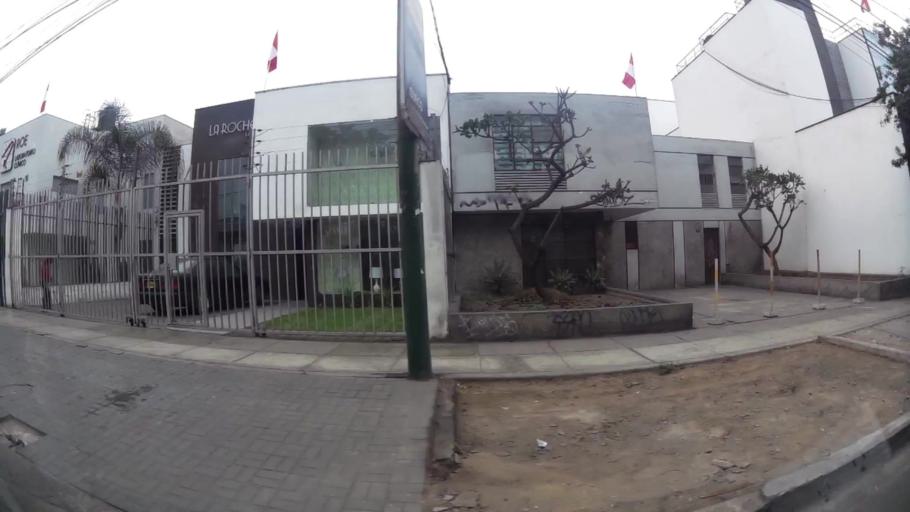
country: PE
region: Lima
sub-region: Lima
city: Surco
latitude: -12.1282
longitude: -76.9902
